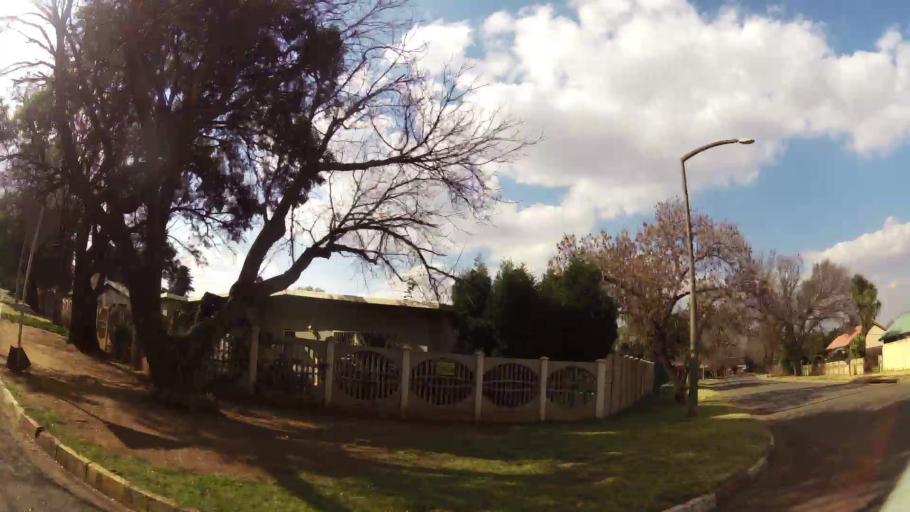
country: ZA
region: Mpumalanga
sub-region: Nkangala District Municipality
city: Delmas
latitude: -26.1414
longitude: 28.6751
